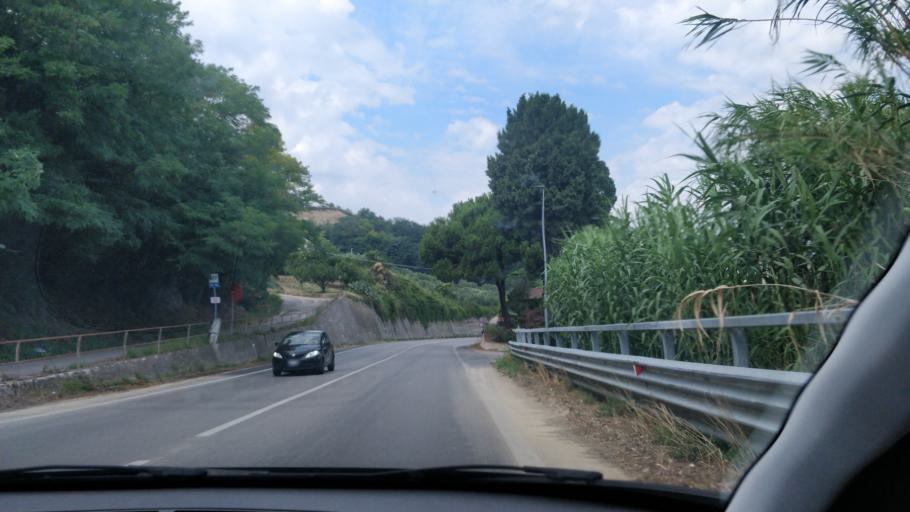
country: IT
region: Abruzzo
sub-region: Provincia di Chieti
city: Marina di San Vito
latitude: 42.3197
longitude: 14.4306
